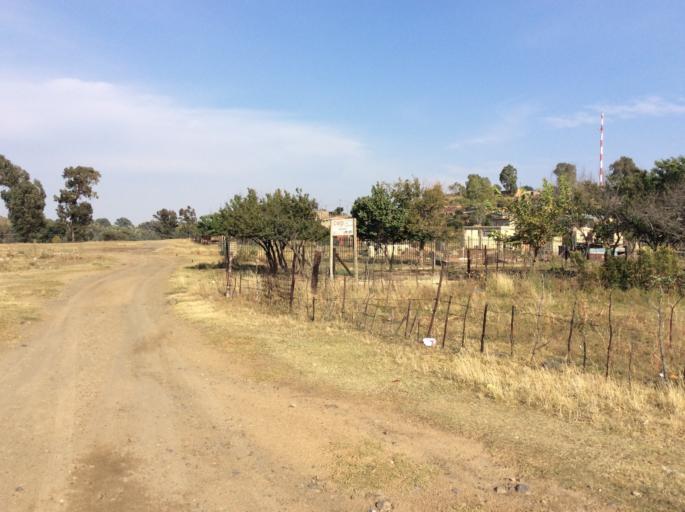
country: LS
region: Mafeteng
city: Mafeteng
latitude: -29.7229
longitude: 27.0364
